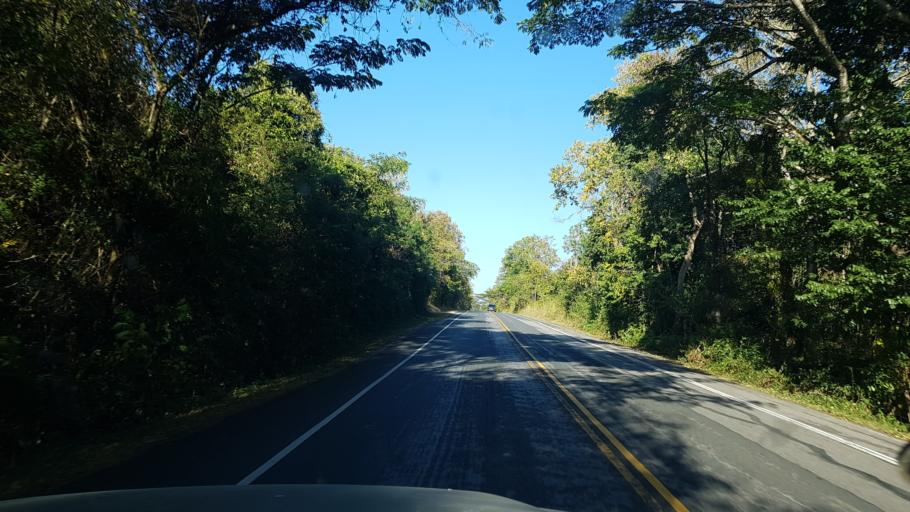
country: TH
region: Phetchabun
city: Lom Sak
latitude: 16.7473
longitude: 101.4509
